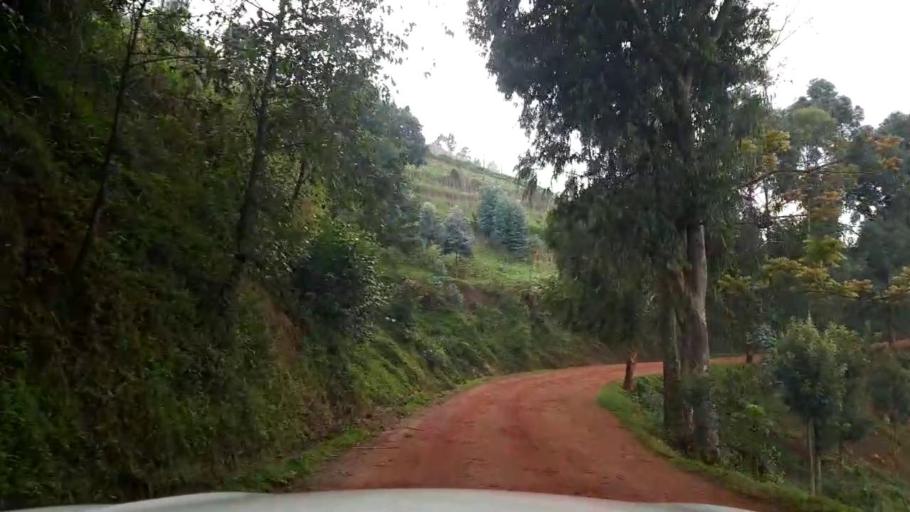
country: UG
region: Western Region
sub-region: Kisoro District
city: Kisoro
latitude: -1.4026
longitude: 29.8011
